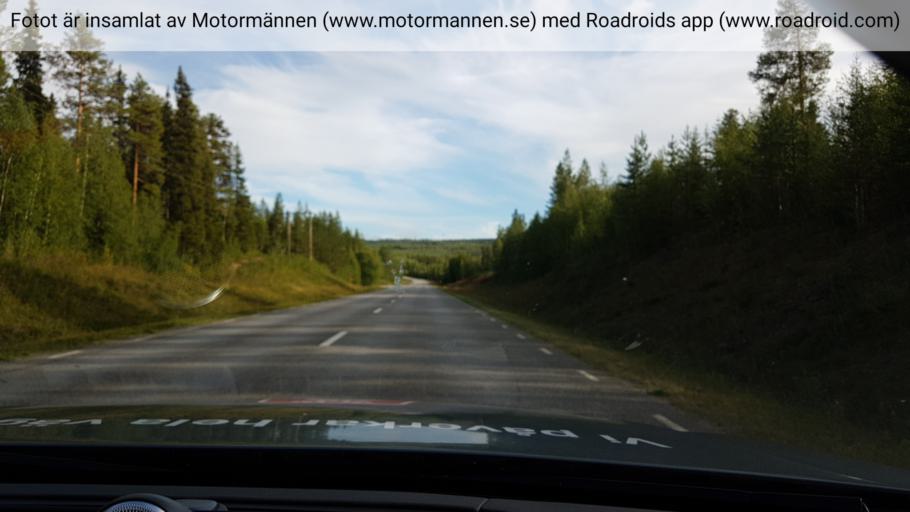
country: SE
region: Jaemtland
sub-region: Stroemsunds Kommun
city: Stroemsund
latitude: 64.2444
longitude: 15.4497
